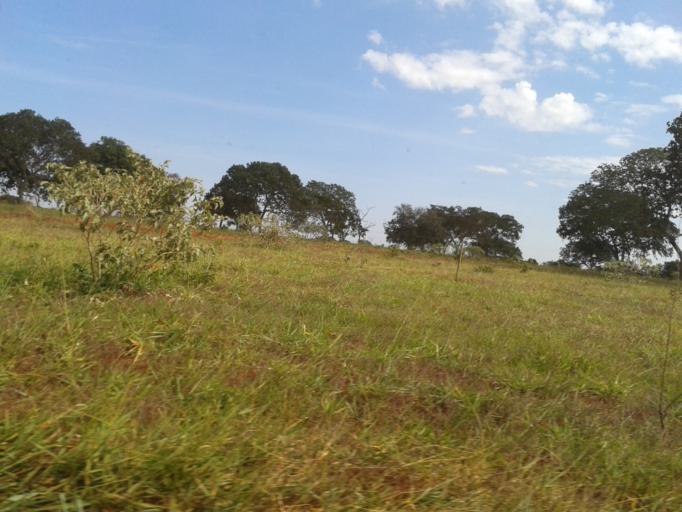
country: BR
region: Minas Gerais
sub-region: Ituiutaba
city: Ituiutaba
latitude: -19.0666
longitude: -49.3645
